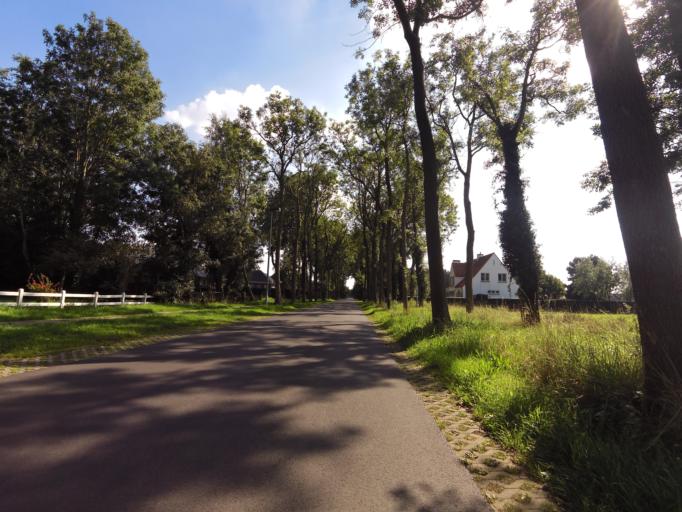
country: BE
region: Flanders
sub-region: Provincie West-Vlaanderen
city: Zedelgem
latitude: 51.1966
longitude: 3.1523
